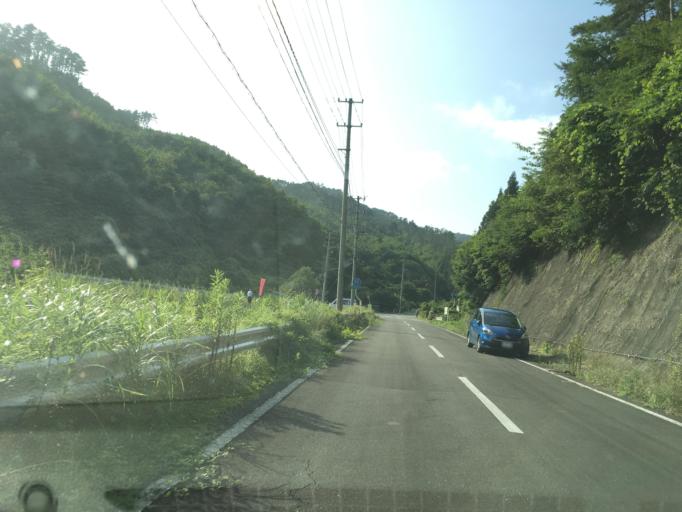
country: JP
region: Iwate
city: Ofunato
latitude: 38.9063
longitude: 141.6226
